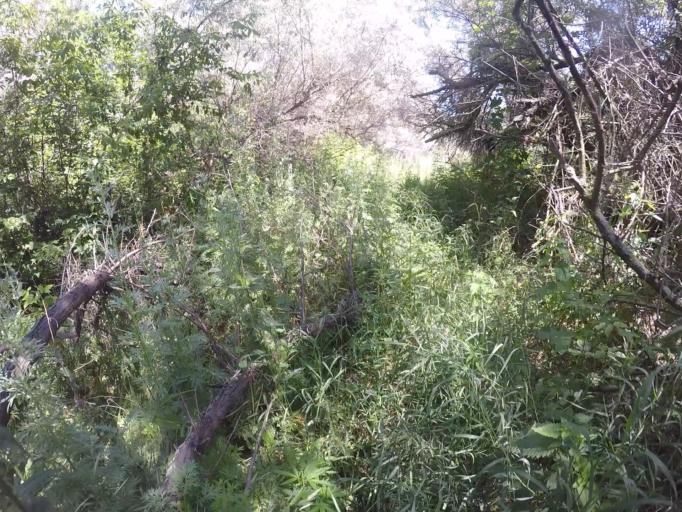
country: RU
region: Saratov
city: Krasnoarmeysk
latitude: 51.1510
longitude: 45.9157
